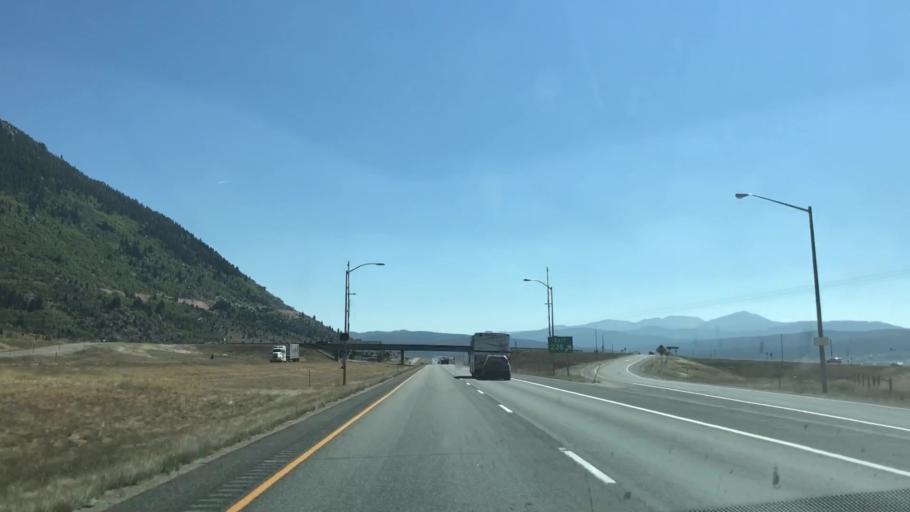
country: US
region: Montana
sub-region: Silver Bow County
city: Butte
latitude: 45.9639
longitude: -112.4735
